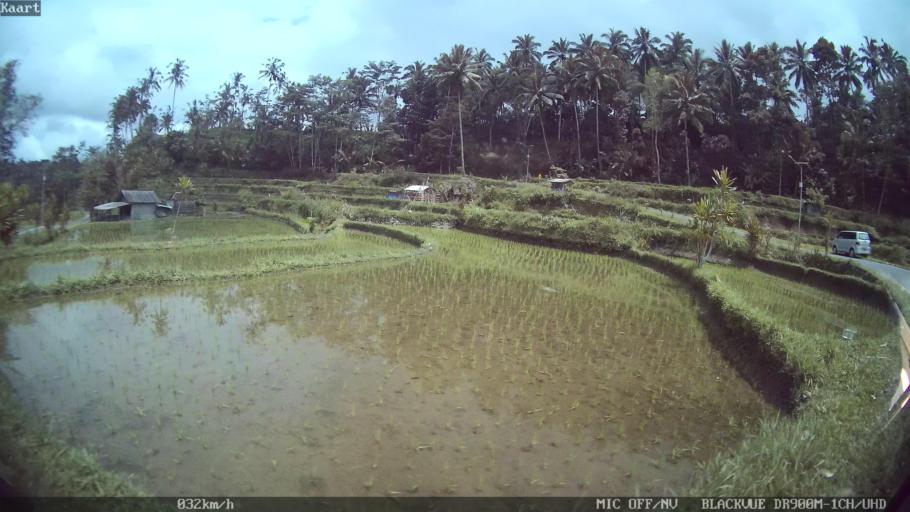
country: ID
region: Bali
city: Banjar Geriana Kangin
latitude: -8.4216
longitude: 115.4376
